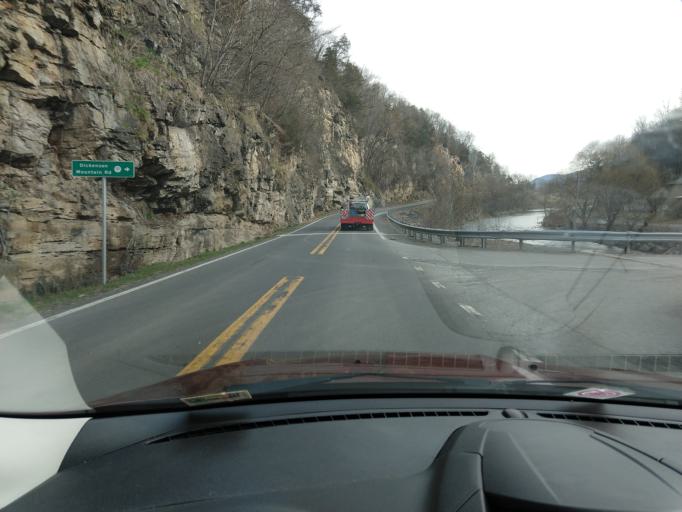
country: US
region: West Virginia
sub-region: Pendleton County
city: Franklin
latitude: 38.6358
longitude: -79.3372
